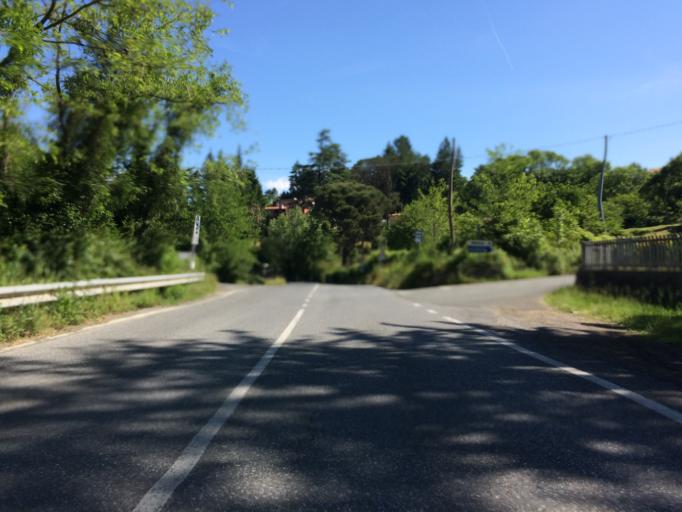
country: IT
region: Tuscany
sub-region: Provincia di Massa-Carrara
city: Montale
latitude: 44.1956
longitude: 9.9514
